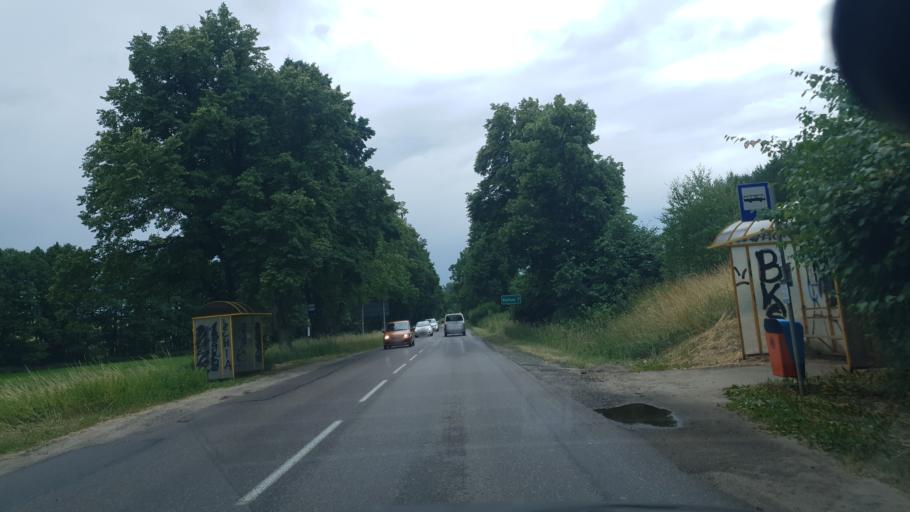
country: PL
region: Pomeranian Voivodeship
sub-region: Powiat kartuski
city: Przodkowo
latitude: 54.3614
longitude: 18.2602
